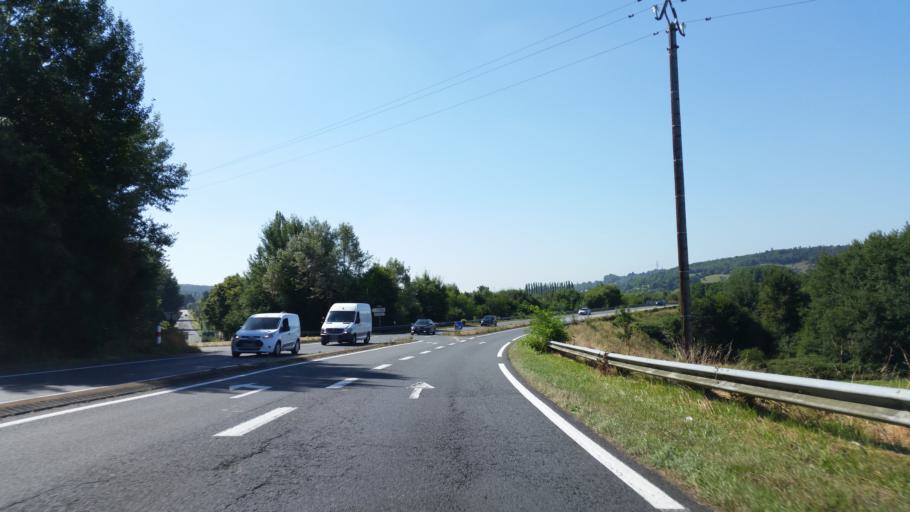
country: FR
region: Lower Normandy
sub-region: Departement du Calvados
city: Lisieux
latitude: 49.2382
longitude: 0.2223
